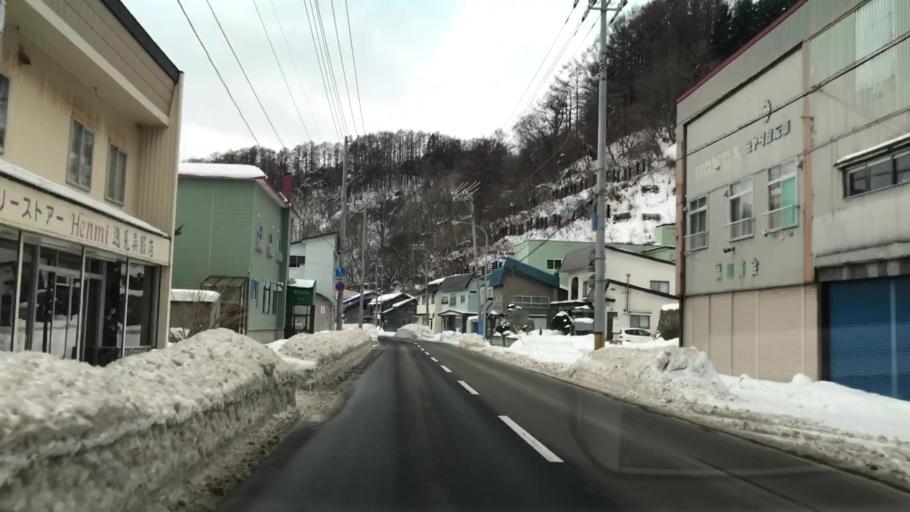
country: JP
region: Hokkaido
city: Yoichi
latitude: 43.2767
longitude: 140.6375
